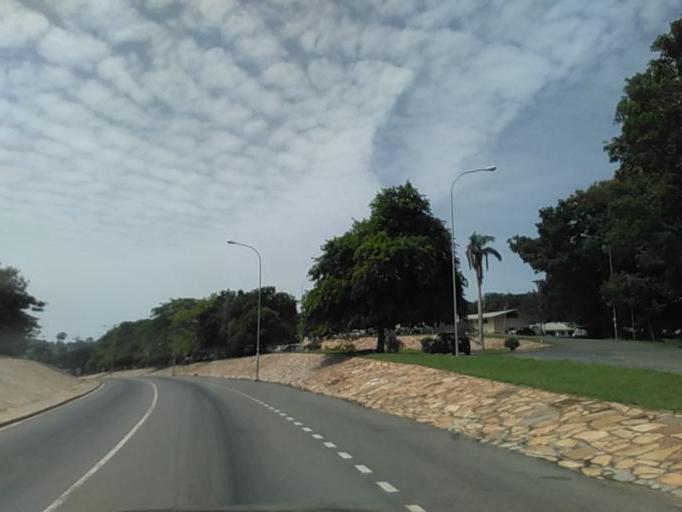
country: GH
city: Akropong
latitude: 6.2653
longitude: 0.0582
